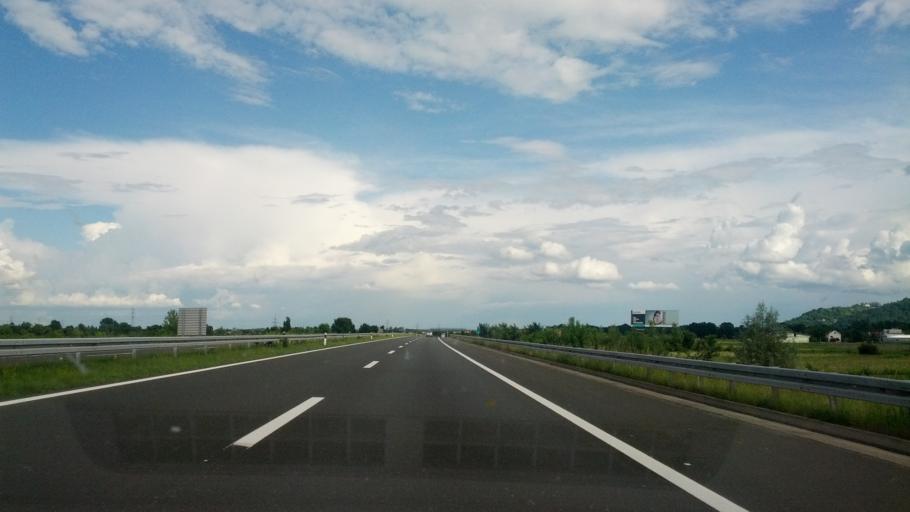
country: HR
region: Zagrebacka
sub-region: Grad Samobor
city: Samobor
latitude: 45.8219
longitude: 15.7480
